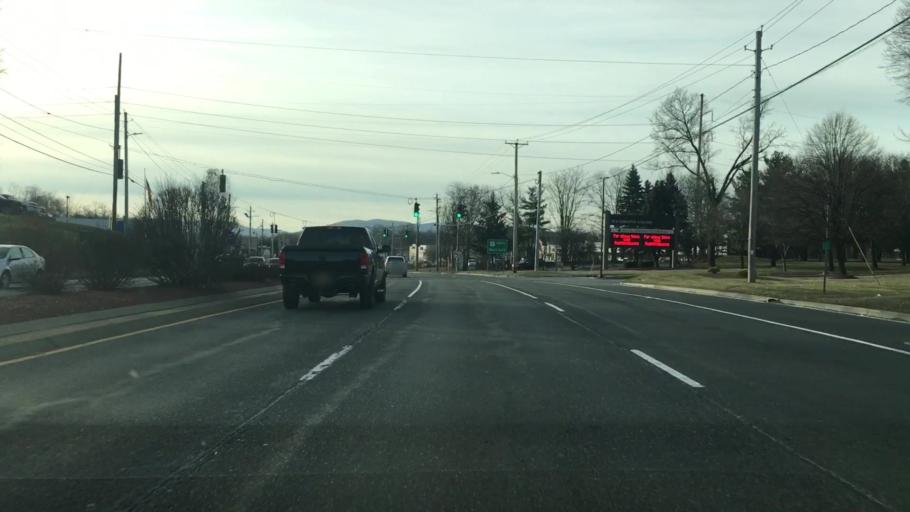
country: US
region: New York
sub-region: Dutchess County
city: Crown Heights
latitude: 41.6250
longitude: -73.9177
